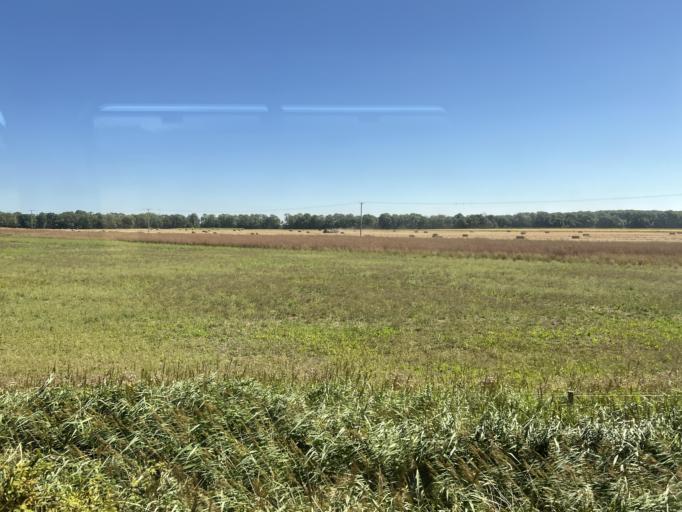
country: GB
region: England
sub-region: Lincolnshire
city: Spilsby
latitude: 53.1125
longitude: 0.1264
